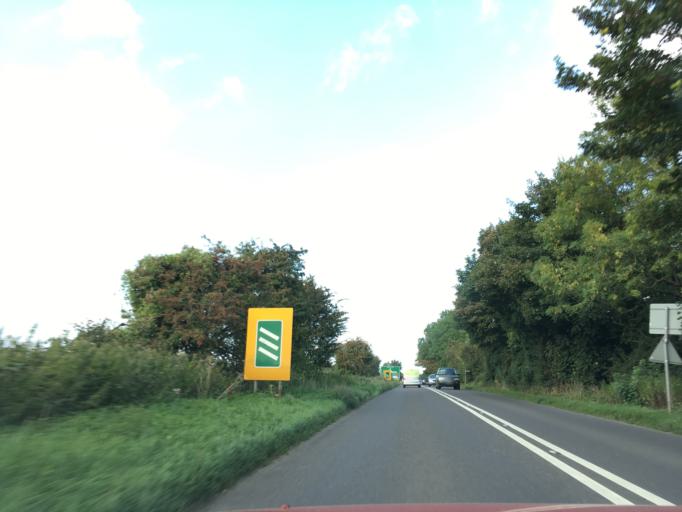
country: GB
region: England
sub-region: Gloucestershire
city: Northleach
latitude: 51.8358
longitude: -1.8390
